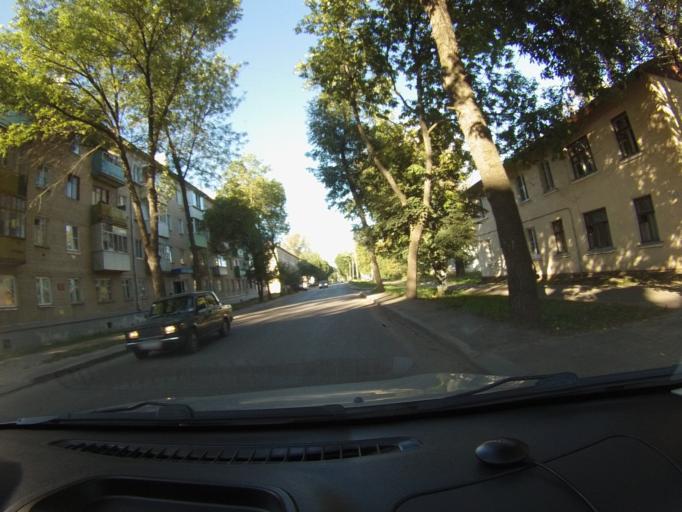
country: RU
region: Tambov
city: Tambov
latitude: 52.7421
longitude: 41.4326
